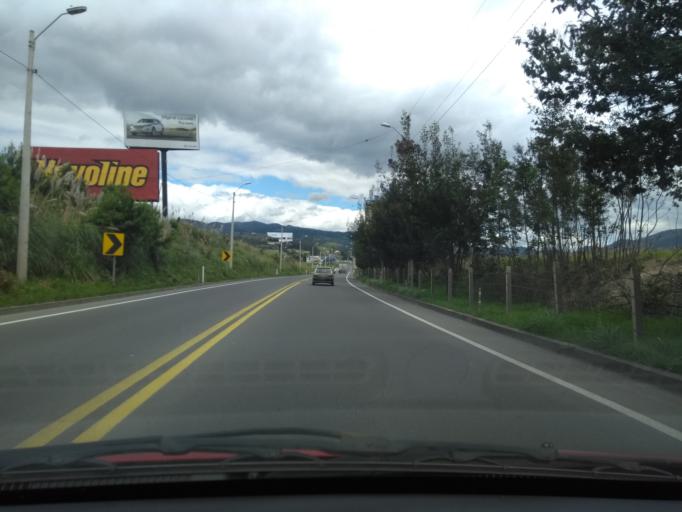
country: EC
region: Azuay
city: Cuenca
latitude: -3.0378
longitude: -79.0420
